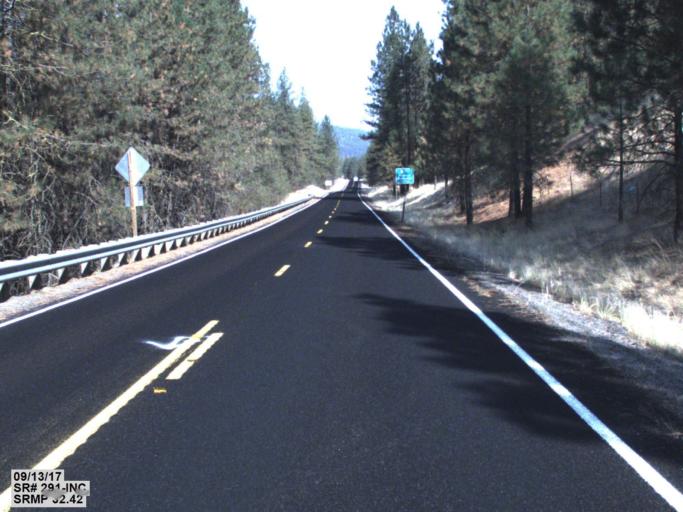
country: US
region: Washington
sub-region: Spokane County
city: Fairchild Air Force Base
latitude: 47.8417
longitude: -117.8454
